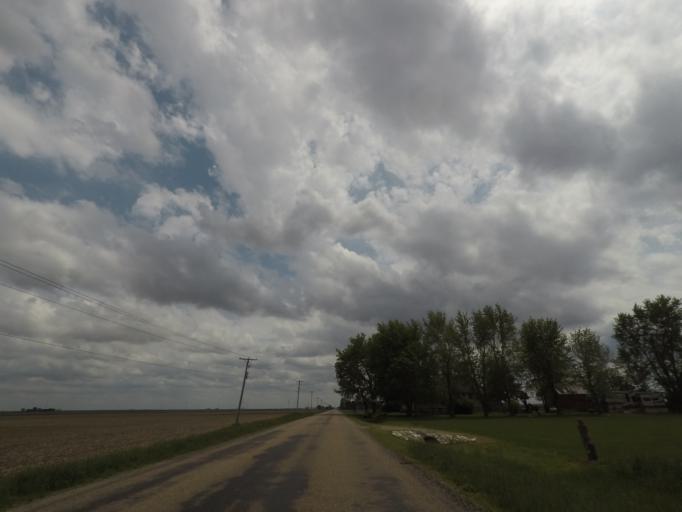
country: US
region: Illinois
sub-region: Macon County
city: Maroa
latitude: 40.0870
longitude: -89.0859
